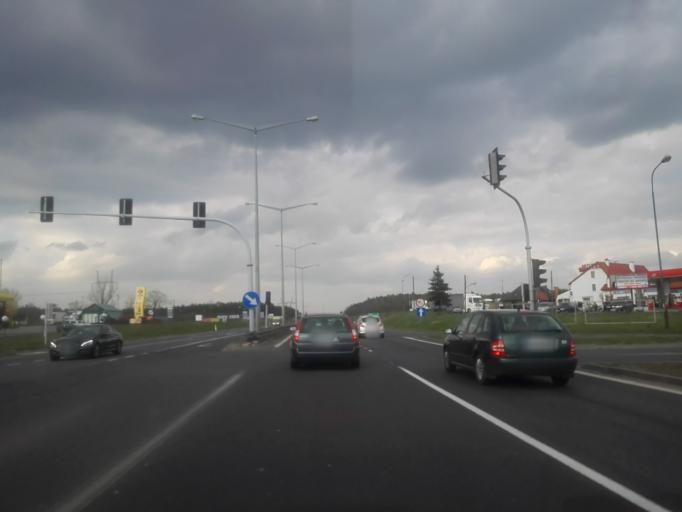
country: PL
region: Lodz Voivodeship
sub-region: Powiat radomszczanski
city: Radomsko
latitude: 51.1066
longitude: 19.3888
